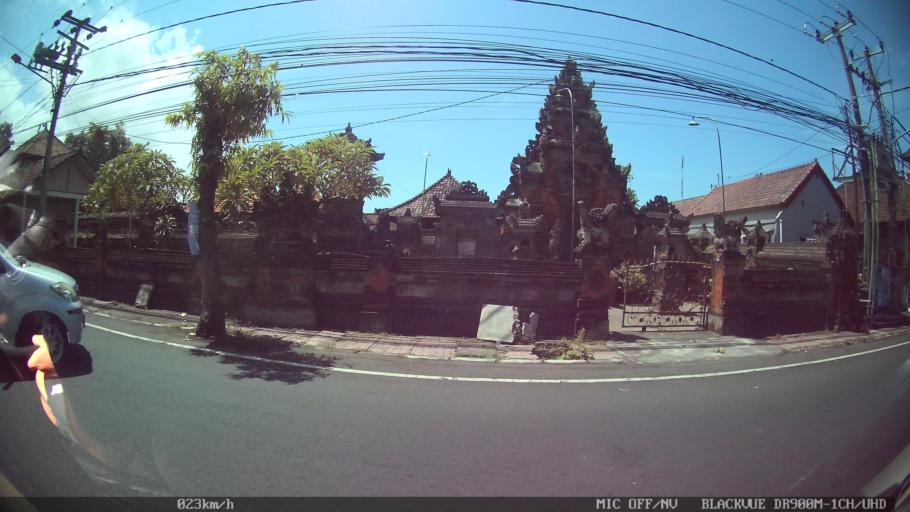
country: ID
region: Bali
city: Banjar Pasekan
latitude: -8.5995
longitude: 115.2830
